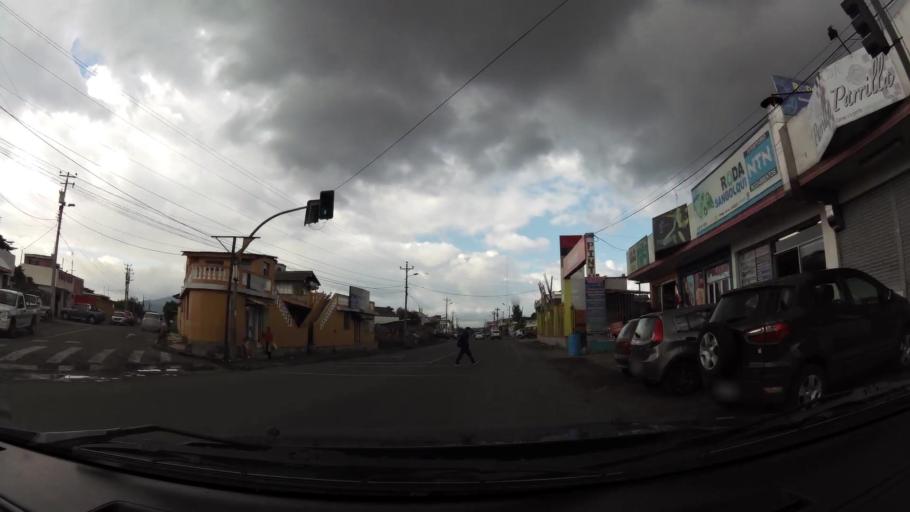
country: EC
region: Pichincha
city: Sangolqui
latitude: -0.3401
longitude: -78.4471
